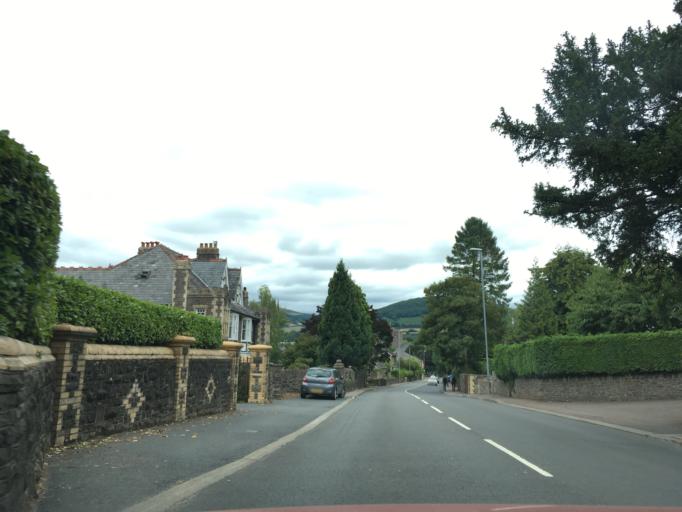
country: GB
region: Wales
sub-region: Monmouthshire
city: Abergavenny
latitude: 51.8172
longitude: -3.0132
